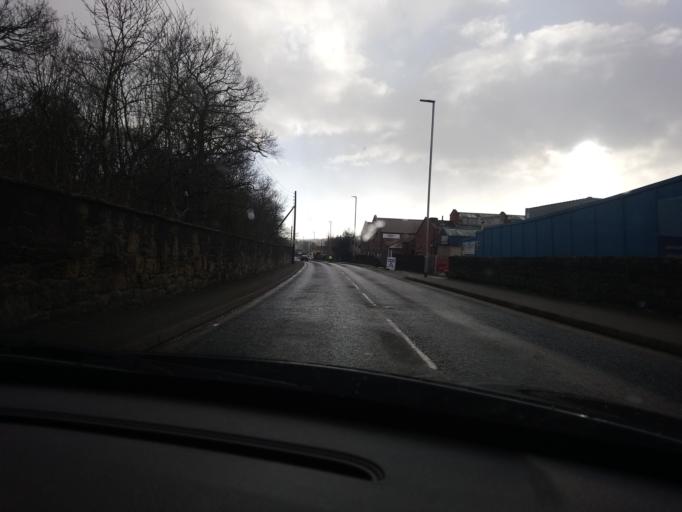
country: GB
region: Wales
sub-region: Wrexham
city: Ruabon
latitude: 52.9747
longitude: -3.0669
